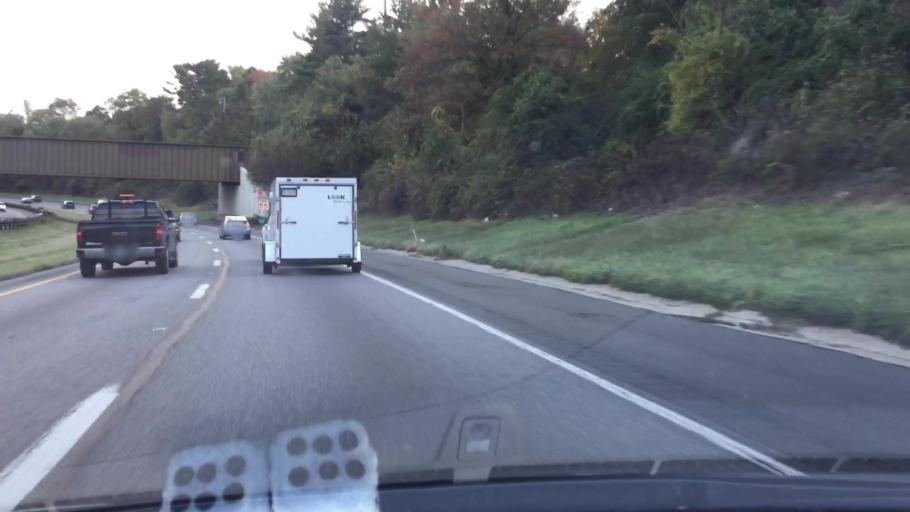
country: US
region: Pennsylvania
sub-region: Delaware County
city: Swarthmore
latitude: 39.9043
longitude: -75.3642
